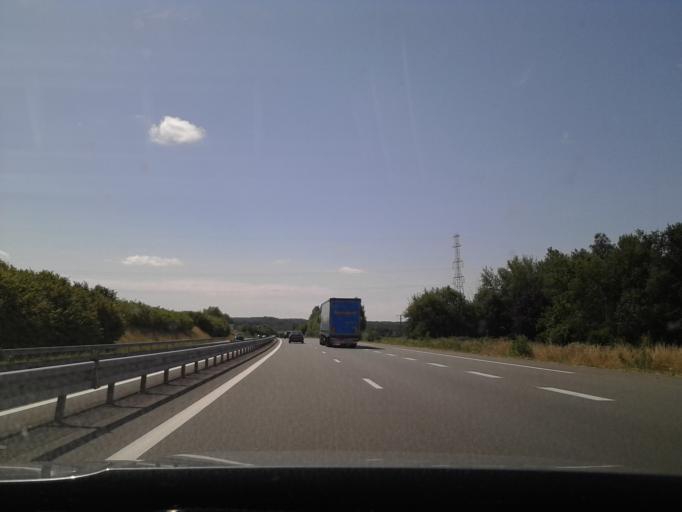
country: FR
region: Pays de la Loire
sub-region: Departement de la Sarthe
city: Teloche
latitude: 47.8796
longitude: 0.3038
